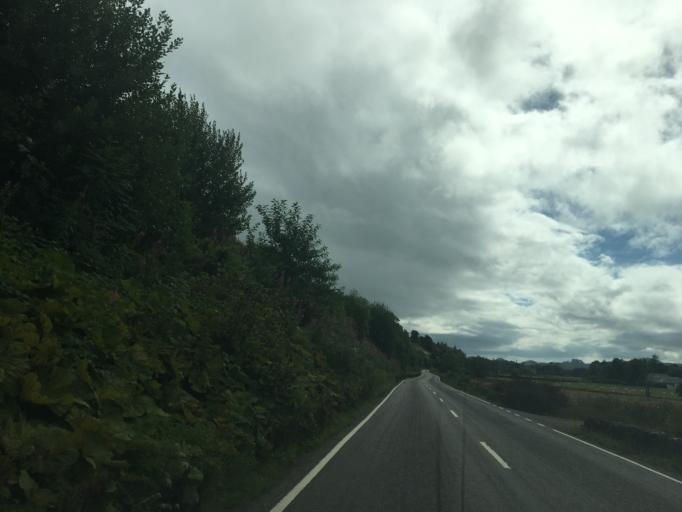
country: GB
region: Scotland
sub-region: Argyll and Bute
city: Lochgilphead
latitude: 56.1290
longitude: -5.4864
